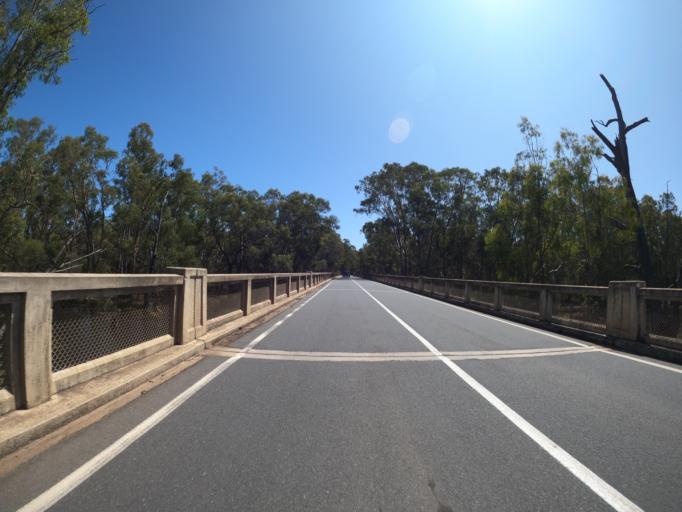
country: AU
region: New South Wales
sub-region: Corowa Shire
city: Corowa
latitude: -36.0686
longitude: 146.2005
